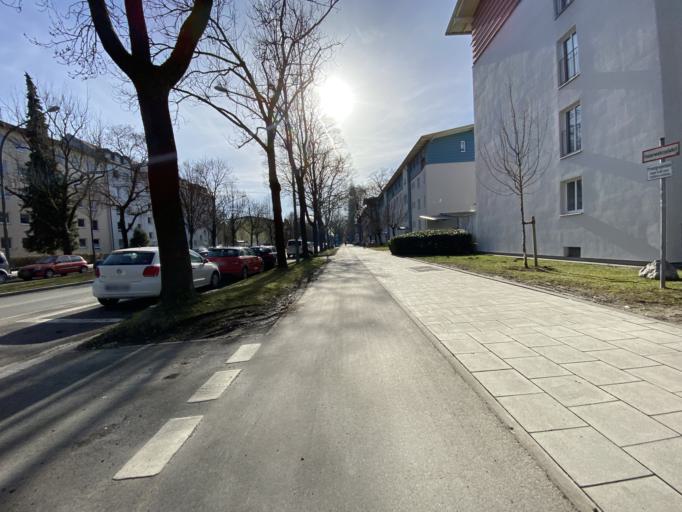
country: DE
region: Bavaria
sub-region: Upper Bavaria
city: Munich
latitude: 48.1085
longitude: 11.5654
